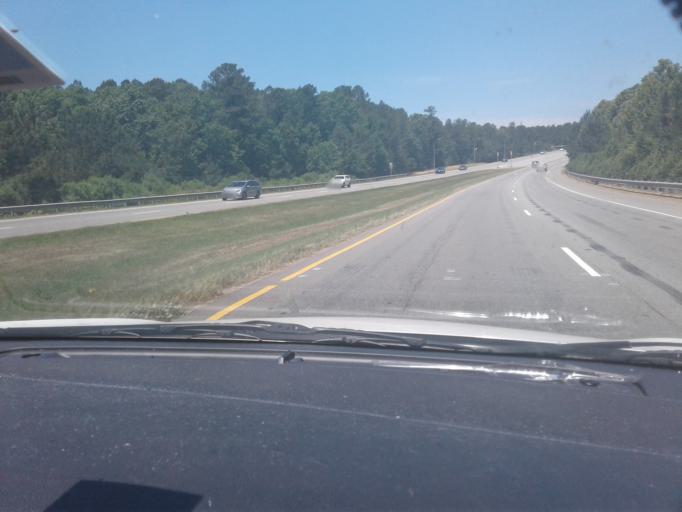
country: US
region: North Carolina
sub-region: Wake County
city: Holly Springs
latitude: 35.6476
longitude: -78.8451
